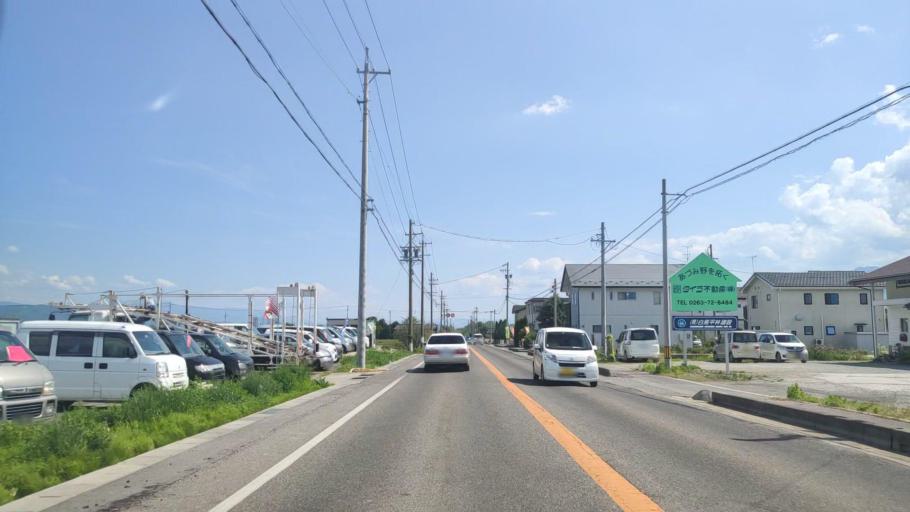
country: JP
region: Nagano
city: Hotaka
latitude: 36.3909
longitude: 137.8642
